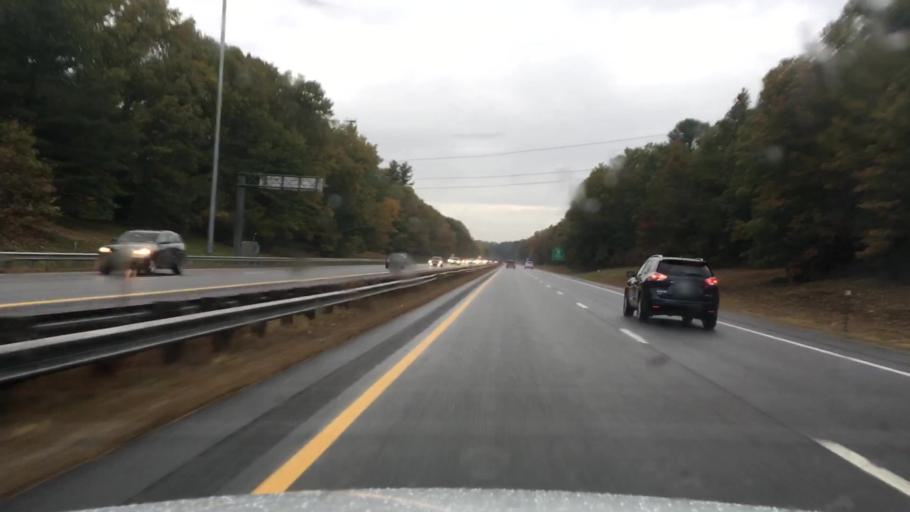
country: US
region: New Hampshire
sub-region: Strafford County
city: Dover
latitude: 43.1649
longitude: -70.8556
